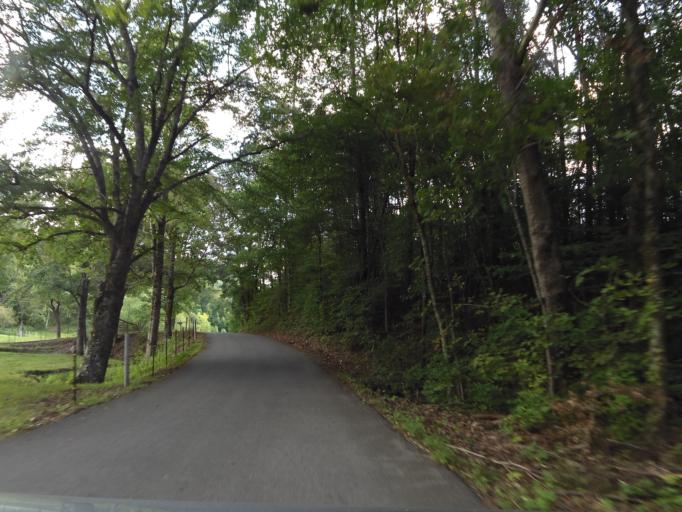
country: US
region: Tennessee
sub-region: Knox County
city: Mascot
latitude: 36.1015
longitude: -83.7650
